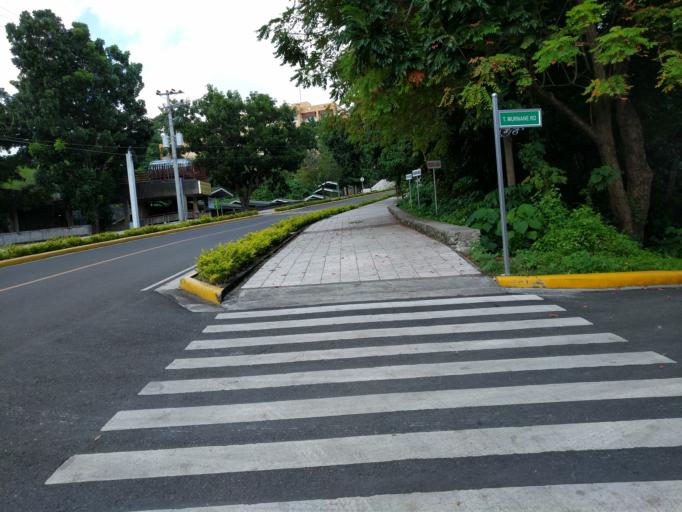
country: PH
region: Central Visayas
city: Mandaue City
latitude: 10.3545
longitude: 123.9121
